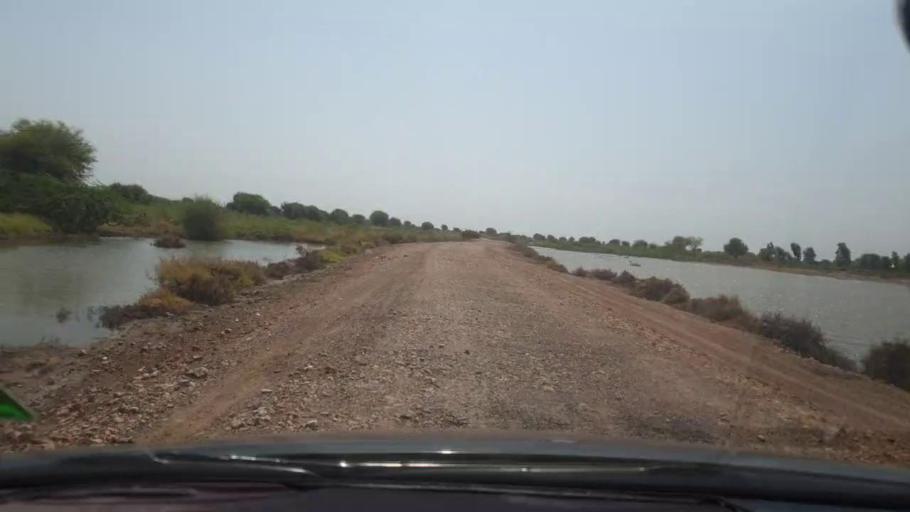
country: PK
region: Sindh
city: Tando Bago
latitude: 24.8090
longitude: 69.1661
